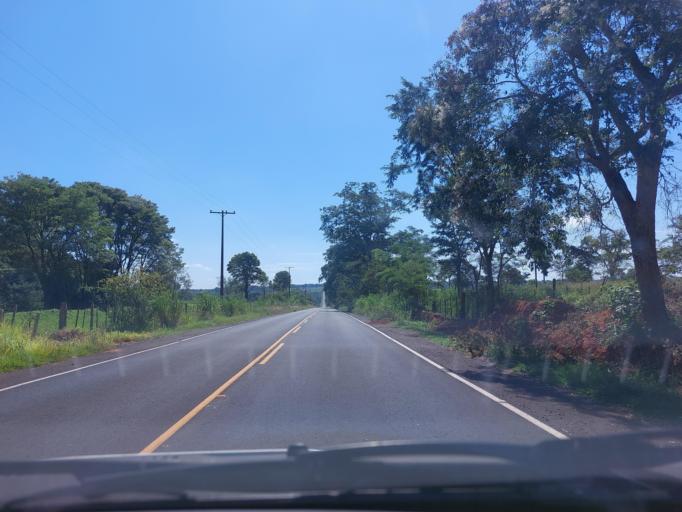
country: PY
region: San Pedro
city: Guayaybi
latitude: -24.5591
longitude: -56.5196
